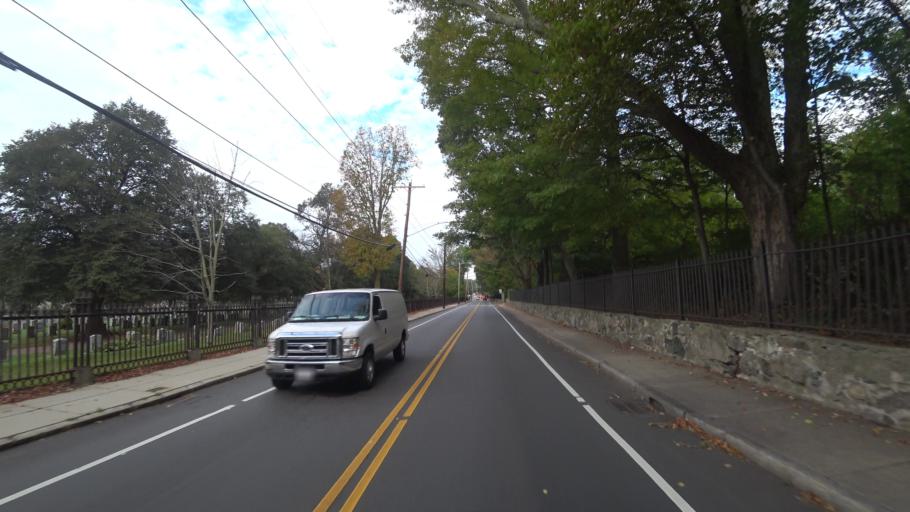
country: US
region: Massachusetts
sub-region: Suffolk County
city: Jamaica Plain
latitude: 42.2852
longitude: -71.1035
